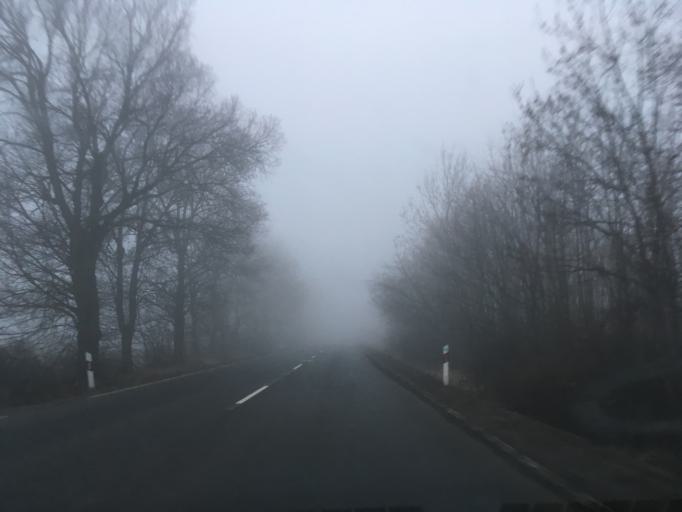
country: HU
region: Heves
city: Kerecsend
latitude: 47.8397
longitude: 20.3674
